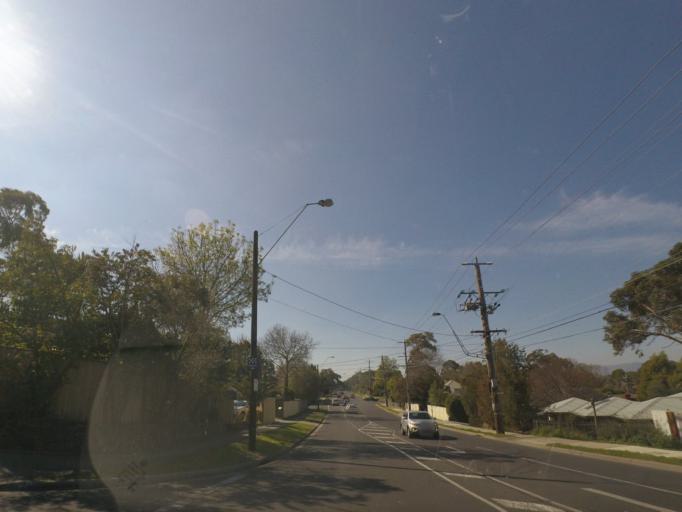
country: AU
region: Victoria
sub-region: Maroondah
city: Ringwood East
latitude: -37.8060
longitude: 145.2260
